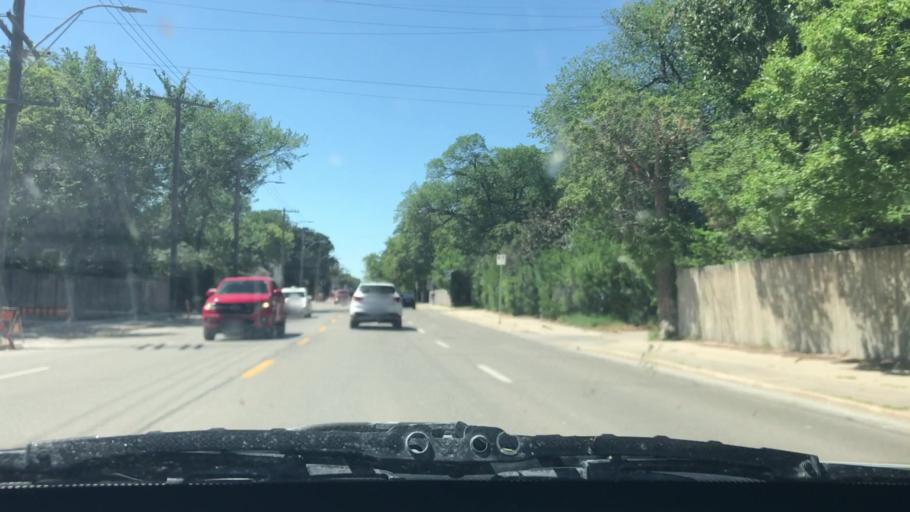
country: CA
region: Manitoba
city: Winnipeg
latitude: 49.8736
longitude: -97.1773
